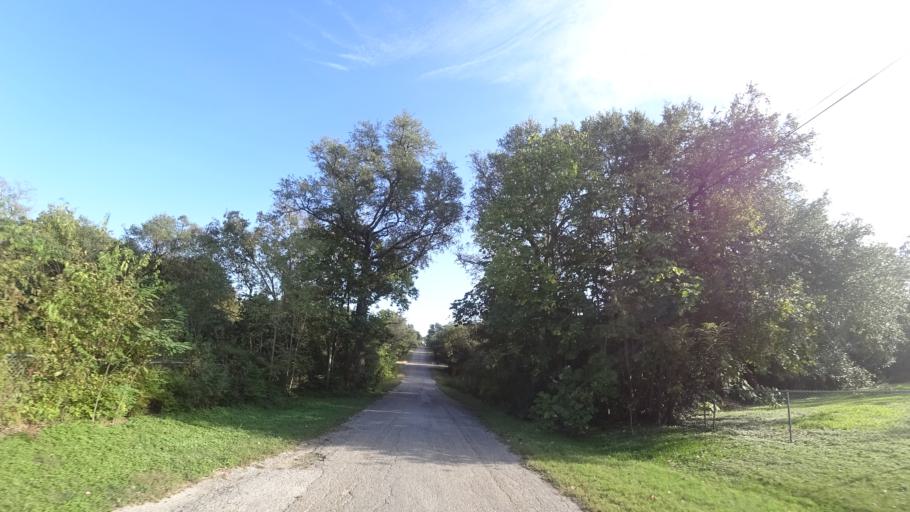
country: US
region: Texas
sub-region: Travis County
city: Barton Creek
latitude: 30.2467
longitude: -97.9200
